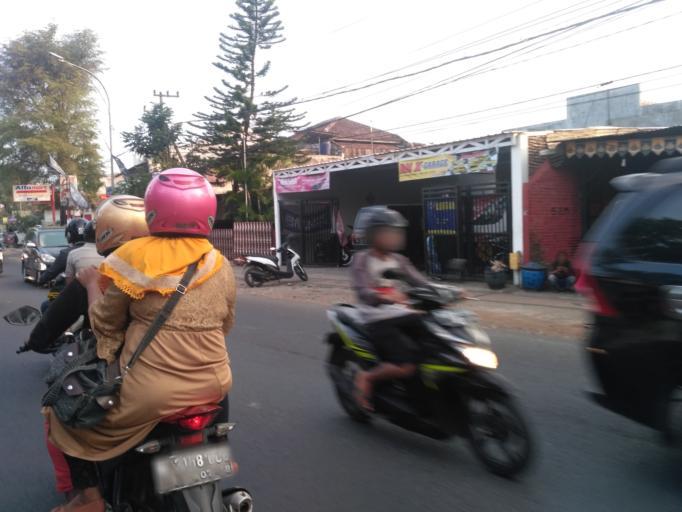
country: ID
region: East Java
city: Kebonsari
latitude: -8.0126
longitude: 112.6204
